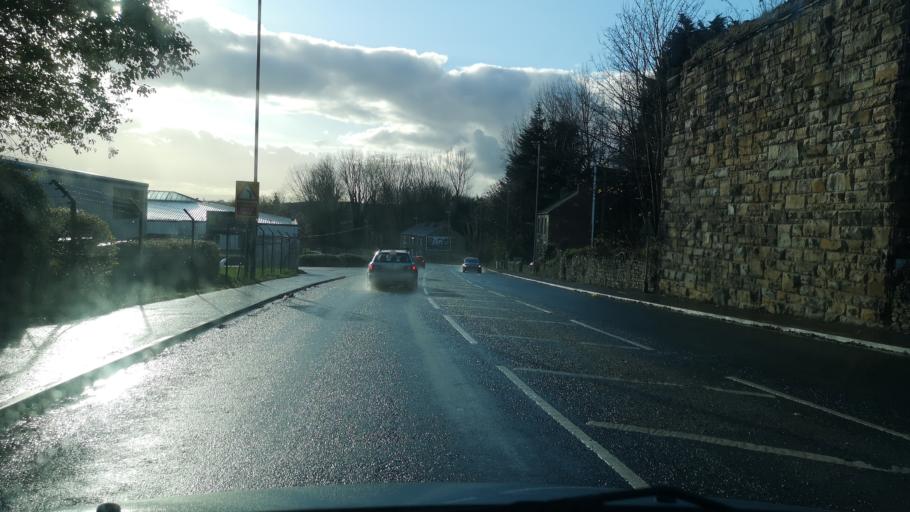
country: GB
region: England
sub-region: City and Borough of Leeds
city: Drighlington
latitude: 53.7365
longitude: -1.6553
